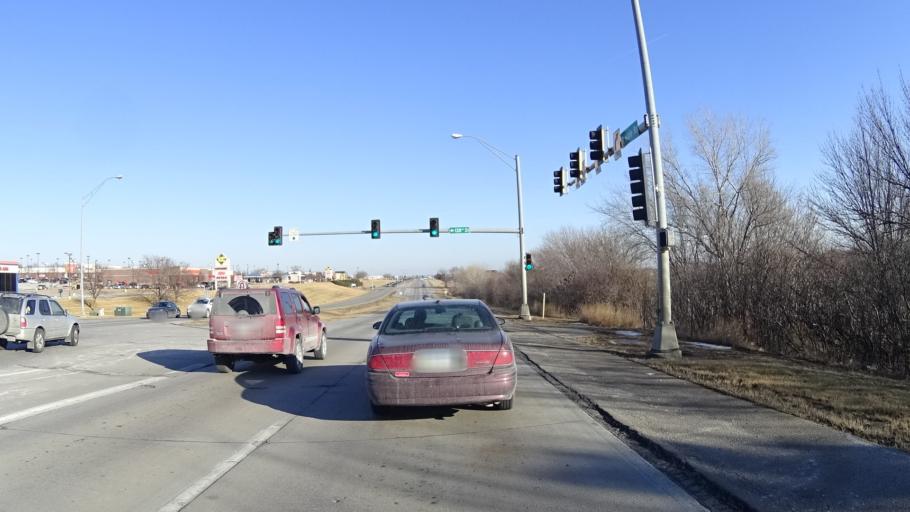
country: US
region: Nebraska
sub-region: Douglas County
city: Bennington
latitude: 41.2919
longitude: -96.1290
